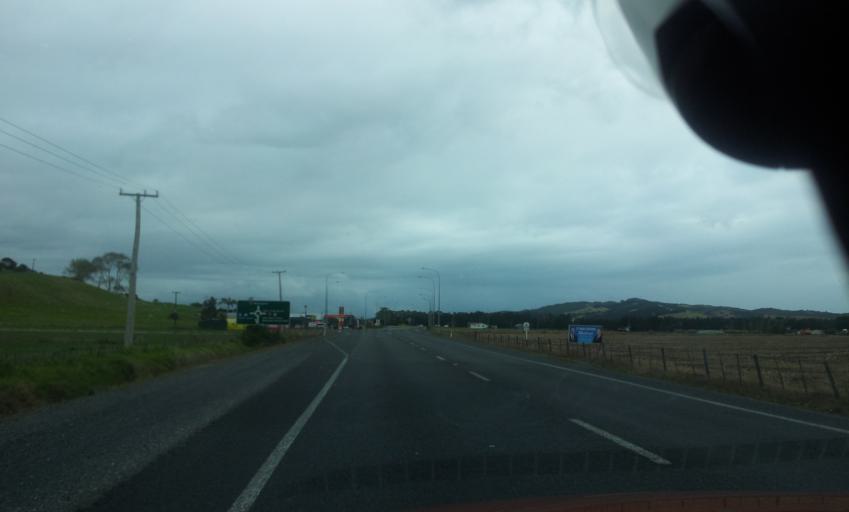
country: NZ
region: Northland
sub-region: Whangarei
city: Ruakaka
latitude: -35.8942
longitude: 174.4362
